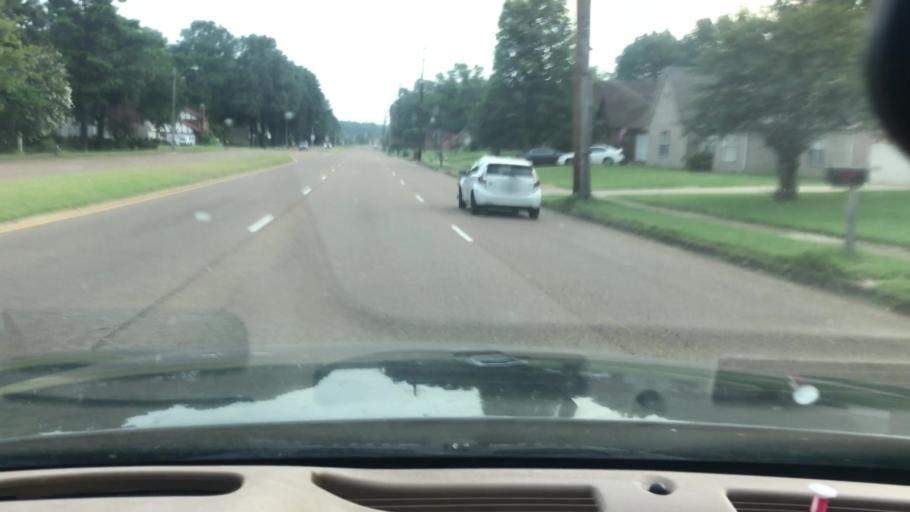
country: US
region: Tennessee
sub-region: Shelby County
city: Bartlett
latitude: 35.1916
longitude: -89.8692
